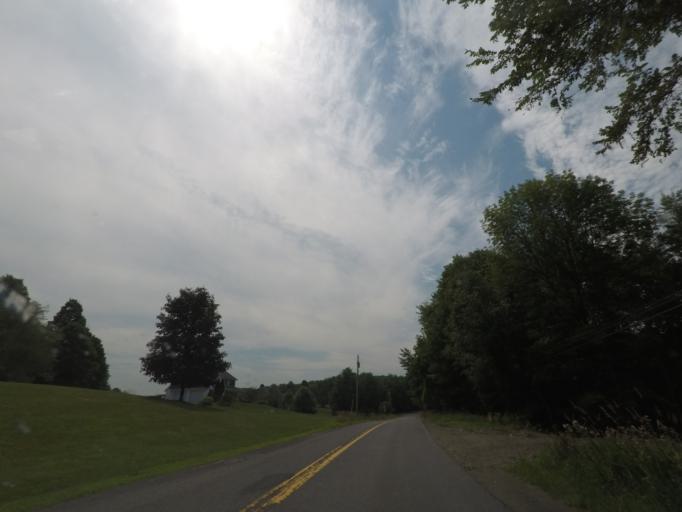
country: US
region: New York
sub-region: Rensselaer County
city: Wynantskill
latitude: 42.7491
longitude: -73.6038
